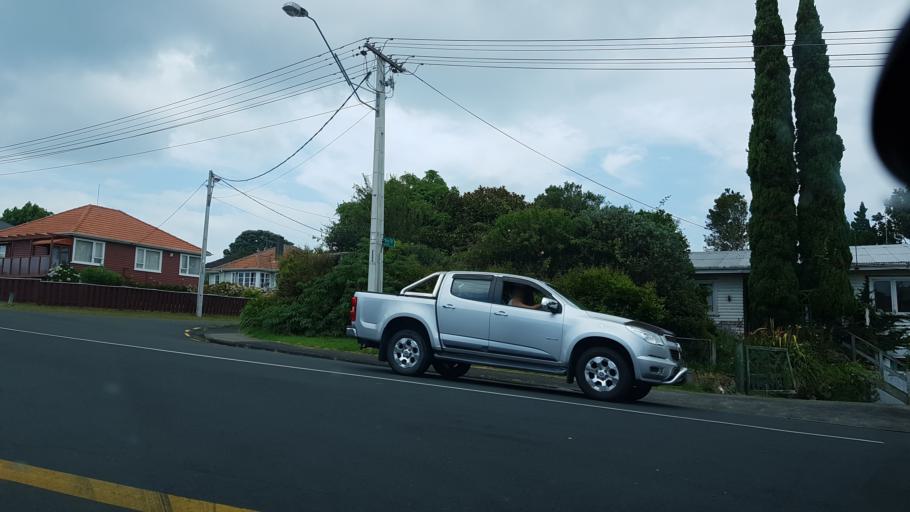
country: NZ
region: Auckland
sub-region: Auckland
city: North Shore
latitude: -36.8059
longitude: 174.7856
